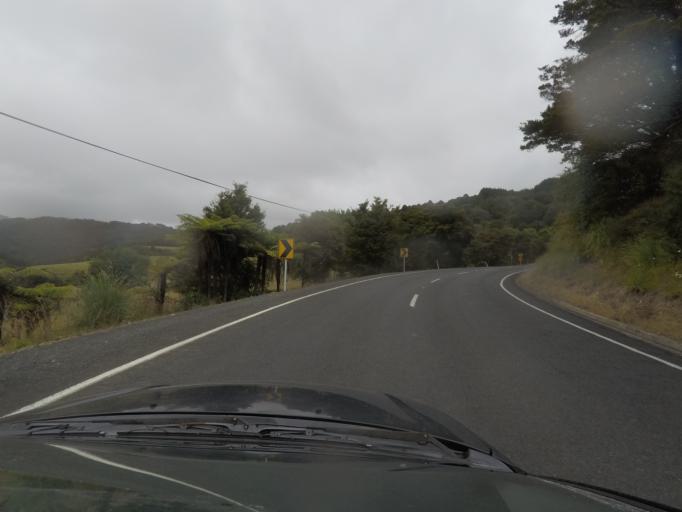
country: NZ
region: Auckland
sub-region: Auckland
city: Warkworth
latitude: -36.2722
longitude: 174.6985
